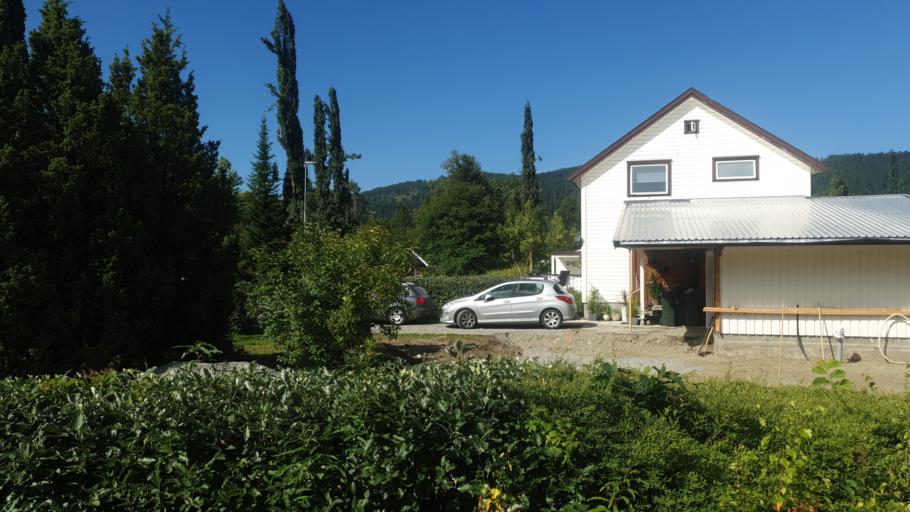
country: NO
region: Sor-Trondelag
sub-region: Orkdal
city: Orkanger
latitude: 63.2880
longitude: 9.8428
